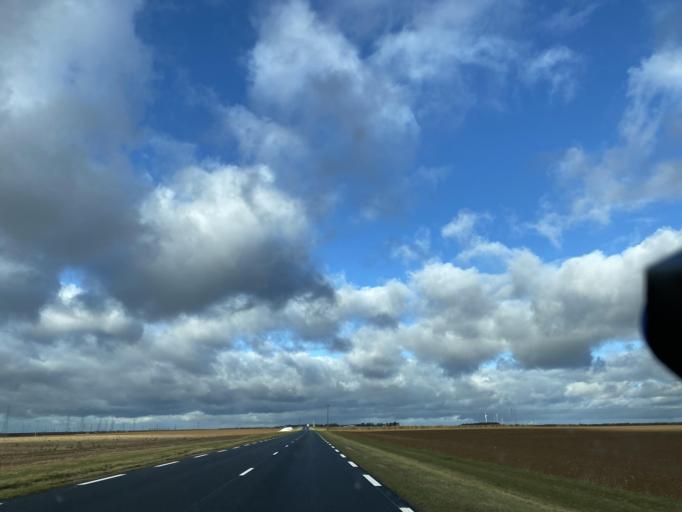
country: FR
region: Centre
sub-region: Departement d'Eure-et-Loir
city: Janville
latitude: 48.1862
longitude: 1.8313
